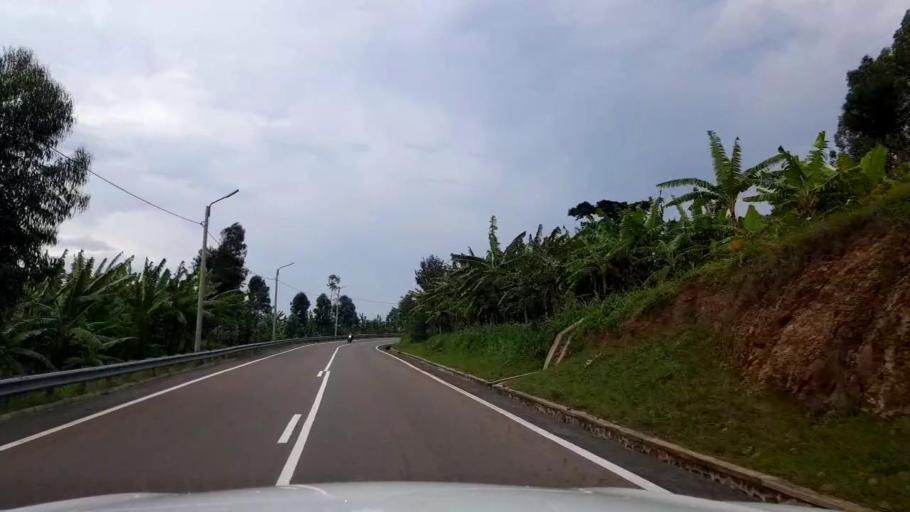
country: RW
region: Western Province
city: Kibuye
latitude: -2.0309
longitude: 29.3960
